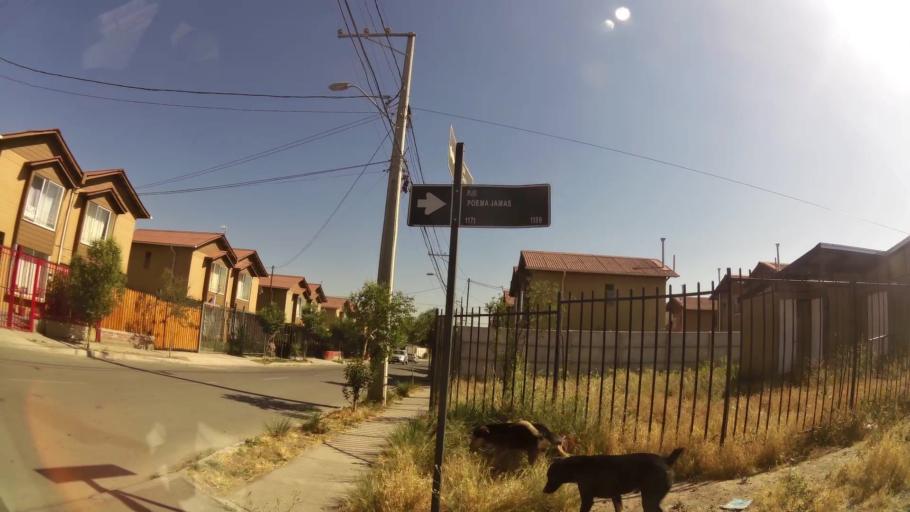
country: CL
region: Santiago Metropolitan
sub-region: Provincia de Maipo
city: San Bernardo
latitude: -33.6101
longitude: -70.6811
